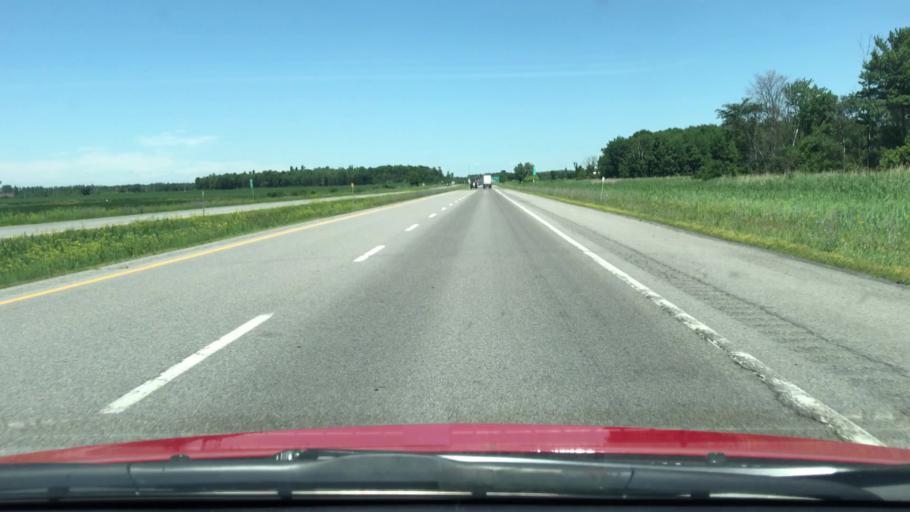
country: CA
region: Quebec
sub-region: Monteregie
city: Napierville
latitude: 45.1771
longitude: -73.4597
